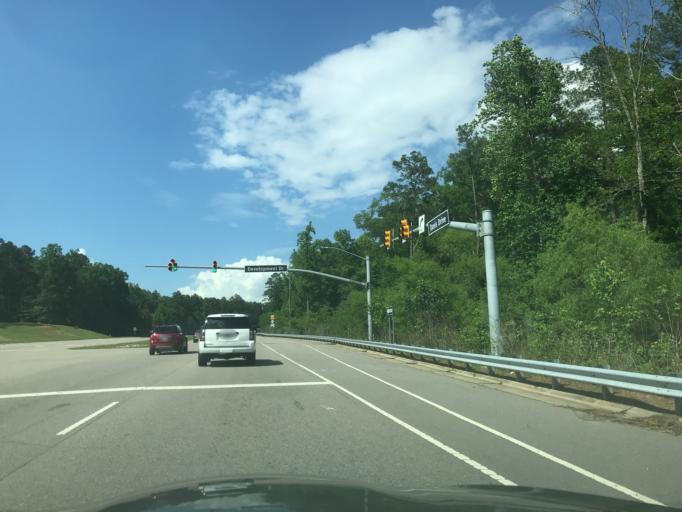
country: US
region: North Carolina
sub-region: Wake County
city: Morrisville
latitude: 35.8659
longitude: -78.8710
